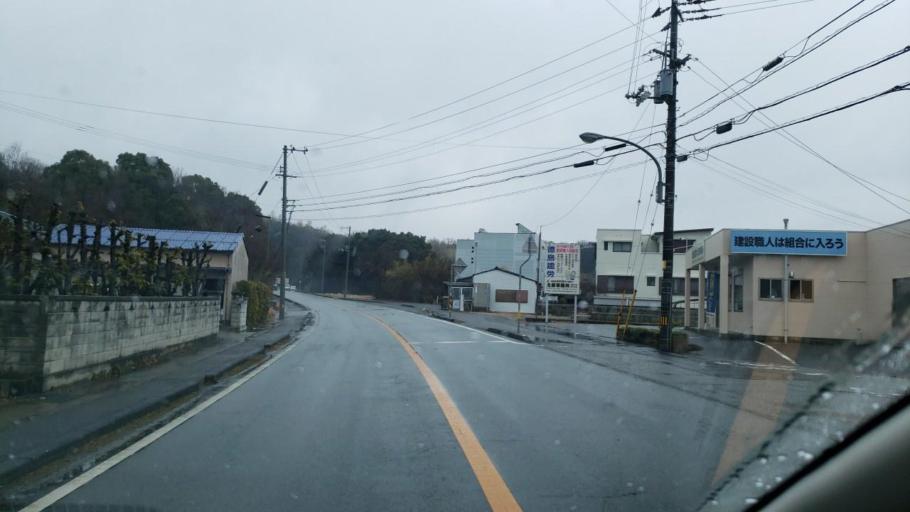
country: JP
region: Tokushima
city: Tokushima-shi
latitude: 34.1552
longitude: 134.5216
